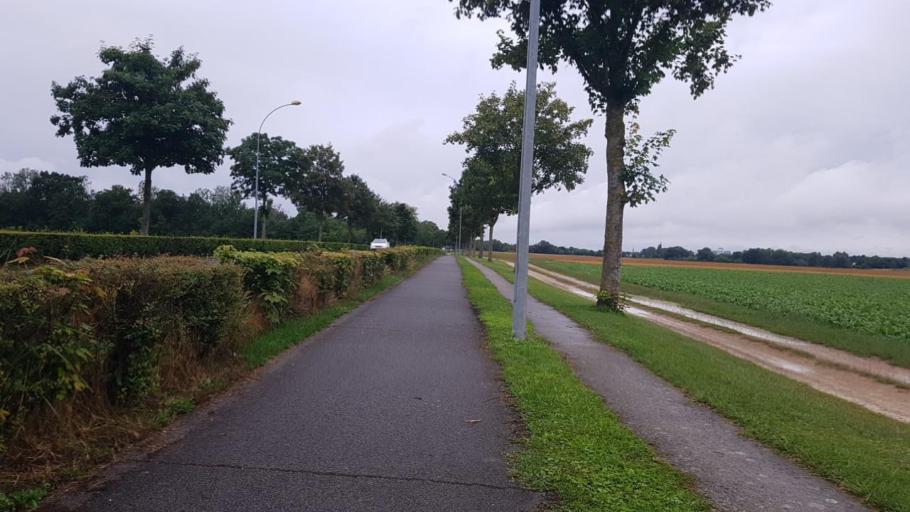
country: FR
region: Champagne-Ardenne
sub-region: Departement de la Marne
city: Sarry
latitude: 48.9262
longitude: 4.3967
